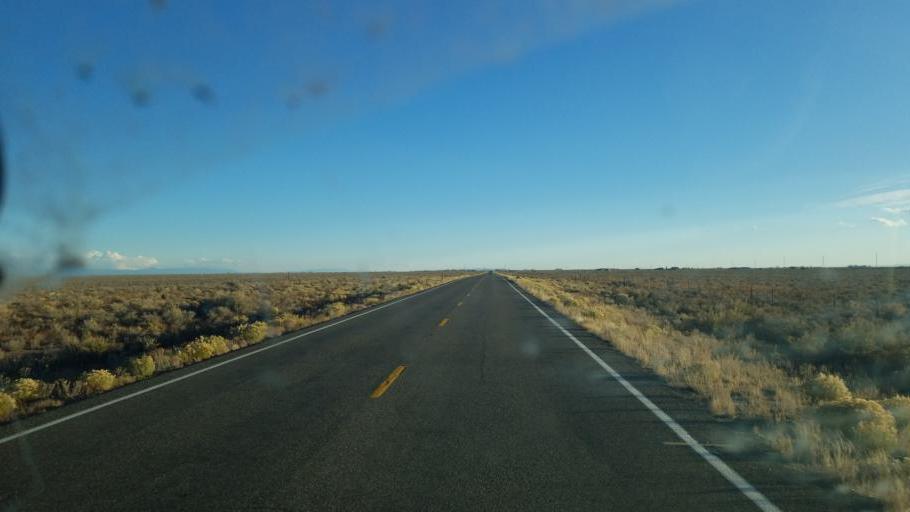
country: US
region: Colorado
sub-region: Saguache County
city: Center
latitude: 37.7986
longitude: -105.8863
